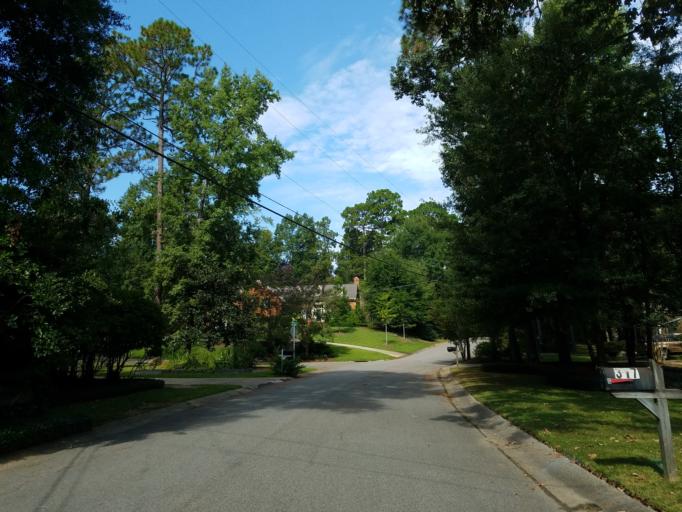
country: US
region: Mississippi
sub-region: Lamar County
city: West Hattiesburg
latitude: 31.3162
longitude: -89.3426
